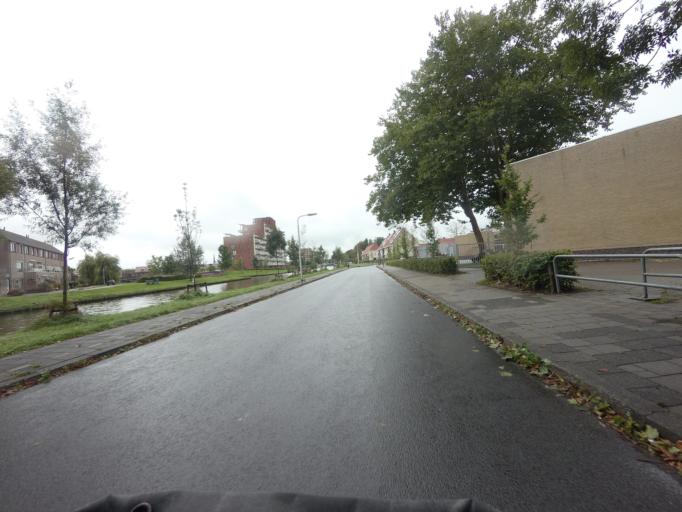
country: NL
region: Friesland
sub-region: Gemeente Leeuwarden
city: Bilgaard
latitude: 53.2157
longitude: 5.8056
